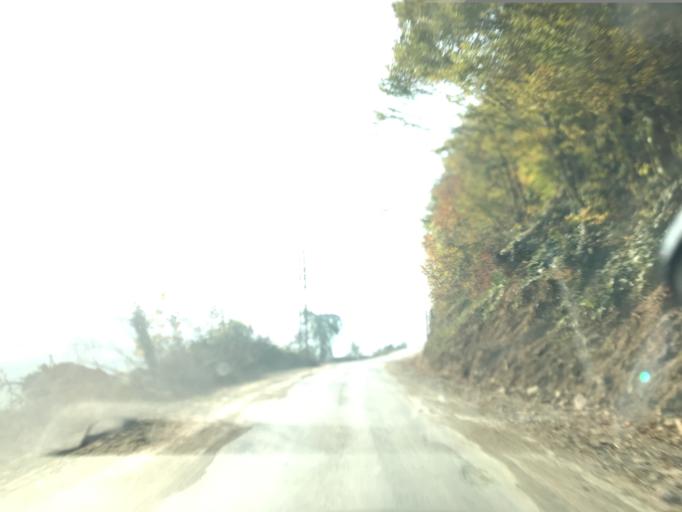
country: TR
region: Duzce
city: Cumayeri
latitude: 40.9262
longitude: 30.9298
